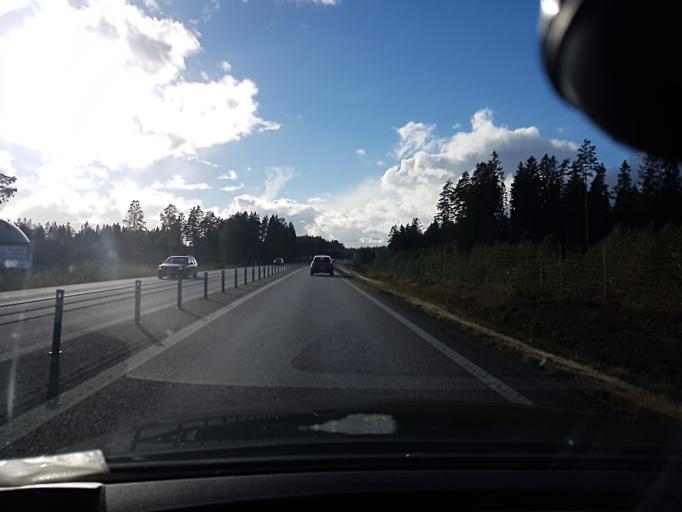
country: SE
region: Kronoberg
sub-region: Alvesta Kommun
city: Alvesta
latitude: 56.9154
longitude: 14.5065
